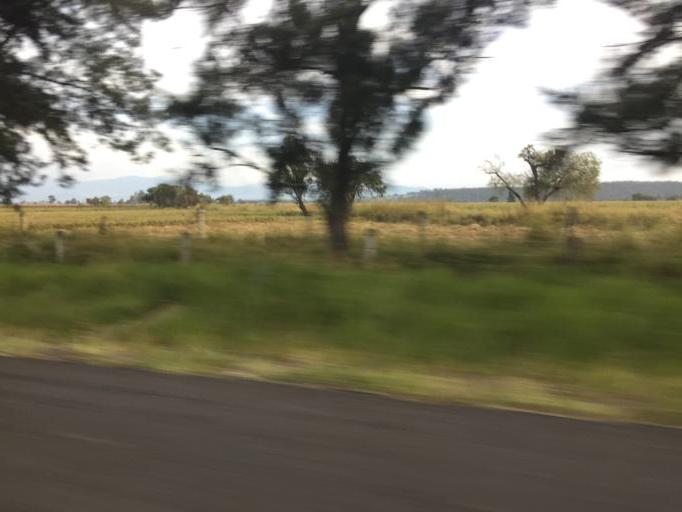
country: MX
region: Michoacan
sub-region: Alvaro Obregon
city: Lazaro Cardenas (La Purisima)
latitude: 19.8913
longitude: -101.0311
